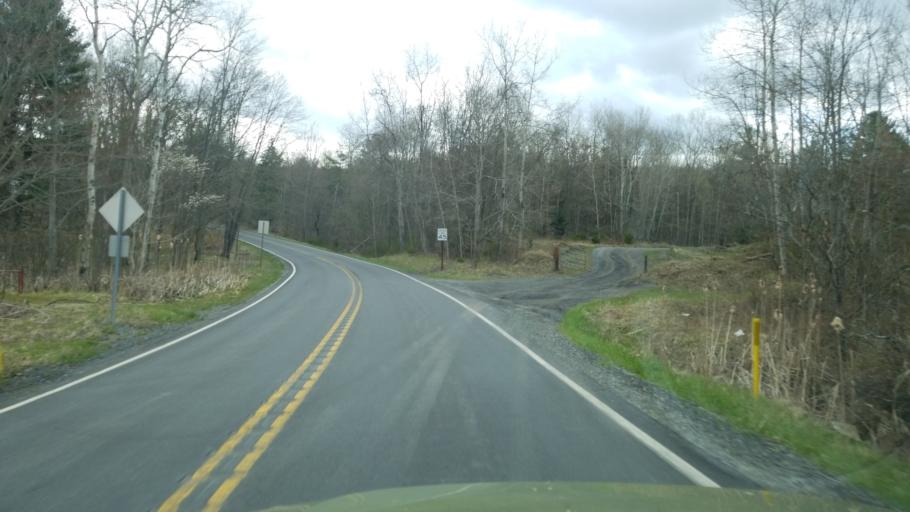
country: US
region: Pennsylvania
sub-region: Clearfield County
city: Curwensville
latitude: 40.8769
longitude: -78.4629
